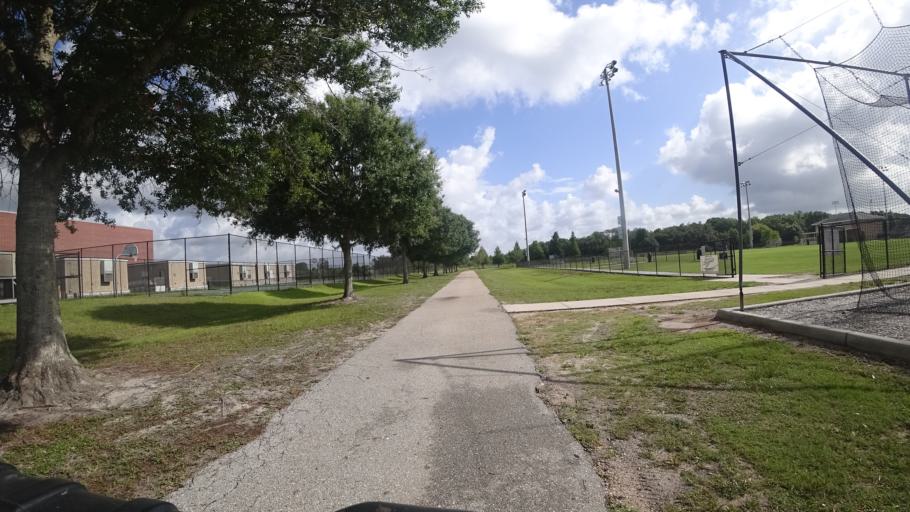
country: US
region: Florida
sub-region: Manatee County
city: Ellenton
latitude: 27.5758
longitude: -82.4874
